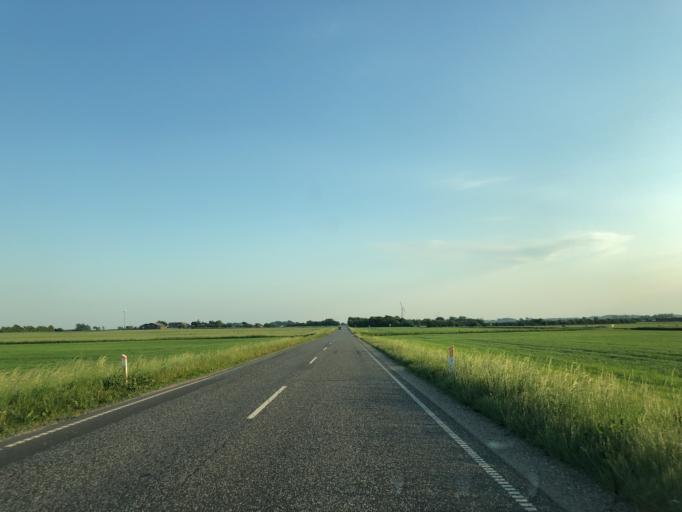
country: DK
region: Central Jutland
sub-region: Struer Kommune
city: Struer
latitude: 56.4539
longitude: 8.5395
